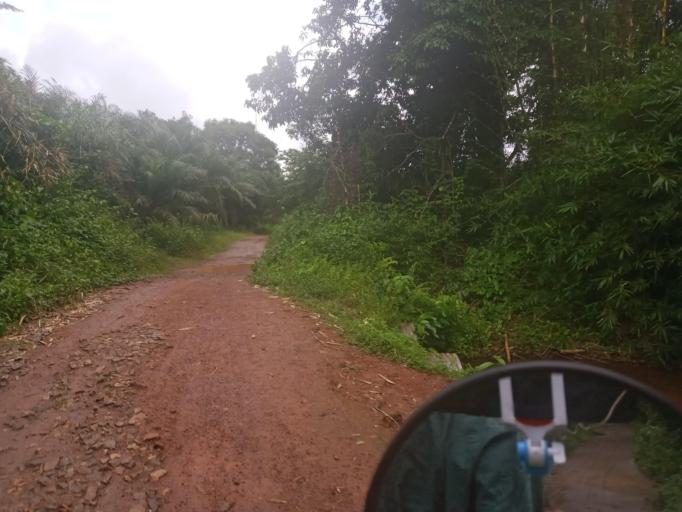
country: SL
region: Northern Province
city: Bumbuna
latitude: 8.9414
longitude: -11.7497
